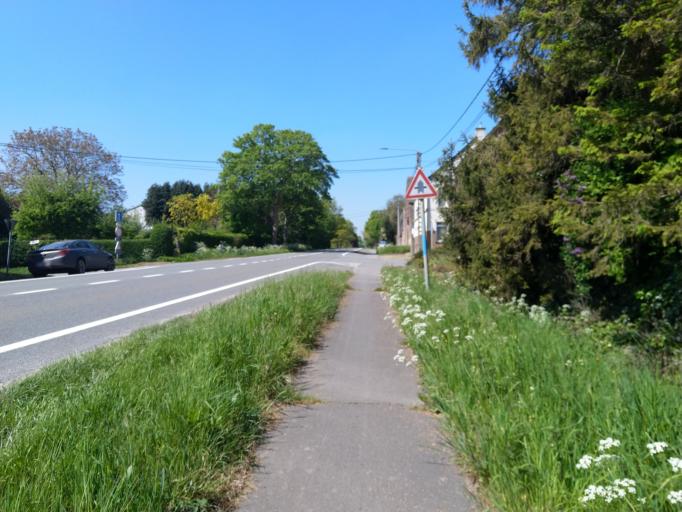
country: BE
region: Wallonia
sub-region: Province du Hainaut
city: Soignies
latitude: 50.6095
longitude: 4.0078
